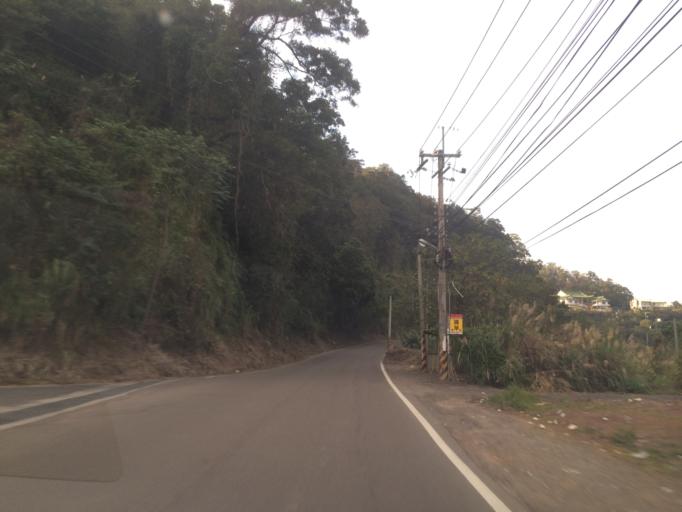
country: TW
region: Taiwan
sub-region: Hsinchu
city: Zhubei
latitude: 24.7009
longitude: 121.0965
